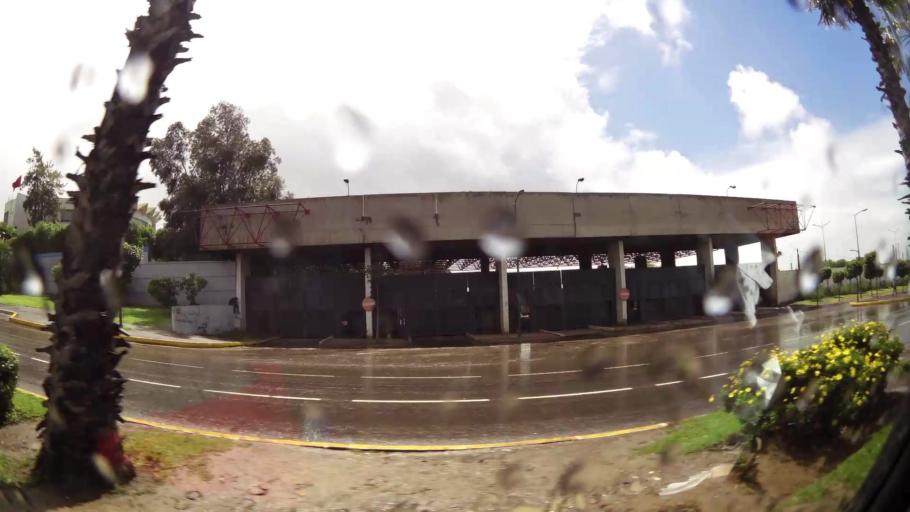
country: MA
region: Grand Casablanca
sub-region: Casablanca
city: Casablanca
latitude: 33.5534
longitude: -7.5544
